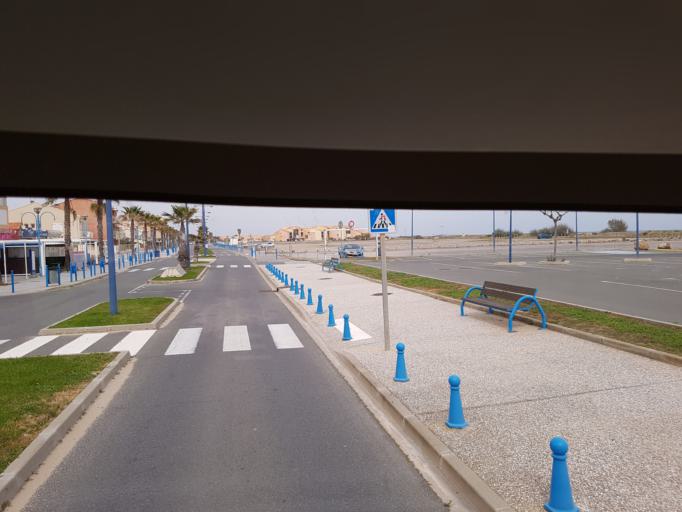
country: FR
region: Languedoc-Roussillon
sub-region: Departement de l'Aude
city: Fleury
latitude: 43.1800
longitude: 3.1917
